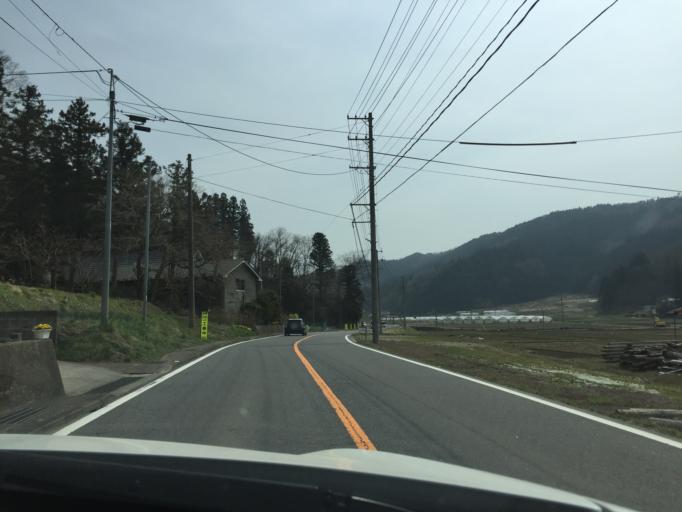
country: JP
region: Fukushima
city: Ishikawa
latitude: 37.1150
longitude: 140.5049
